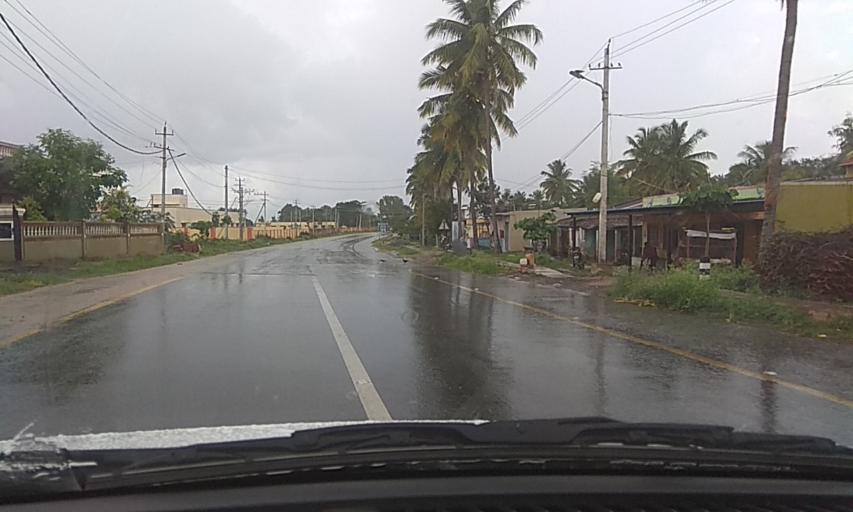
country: IN
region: Karnataka
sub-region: Ramanagara
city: Channapatna
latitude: 12.7693
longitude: 77.0611
